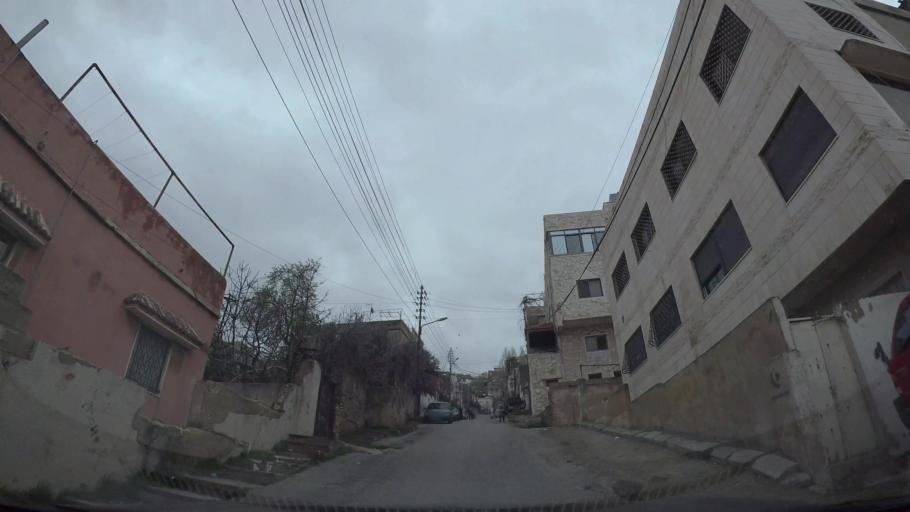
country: JO
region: Amman
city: Wadi as Sir
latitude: 31.9519
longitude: 35.8219
